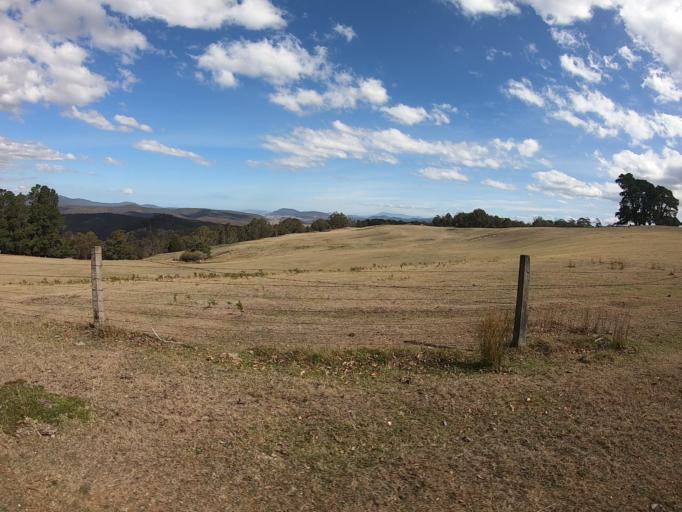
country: AU
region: Tasmania
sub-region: Brighton
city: Bridgewater
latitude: -42.4944
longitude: 147.4171
